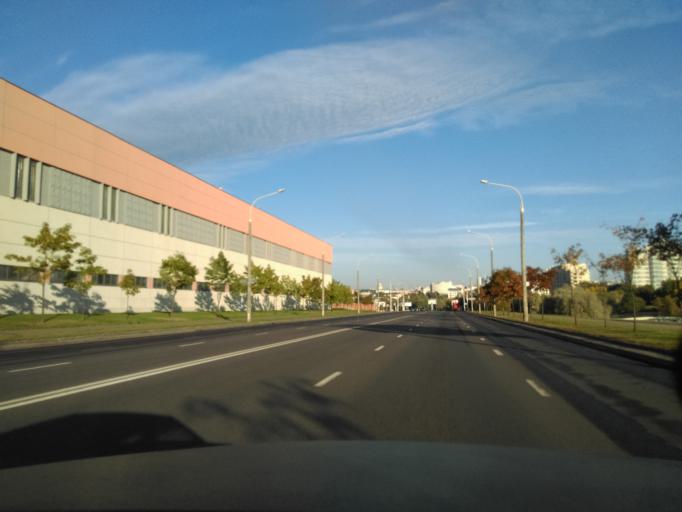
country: BY
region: Minsk
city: Minsk
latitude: 53.8910
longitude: 27.5758
